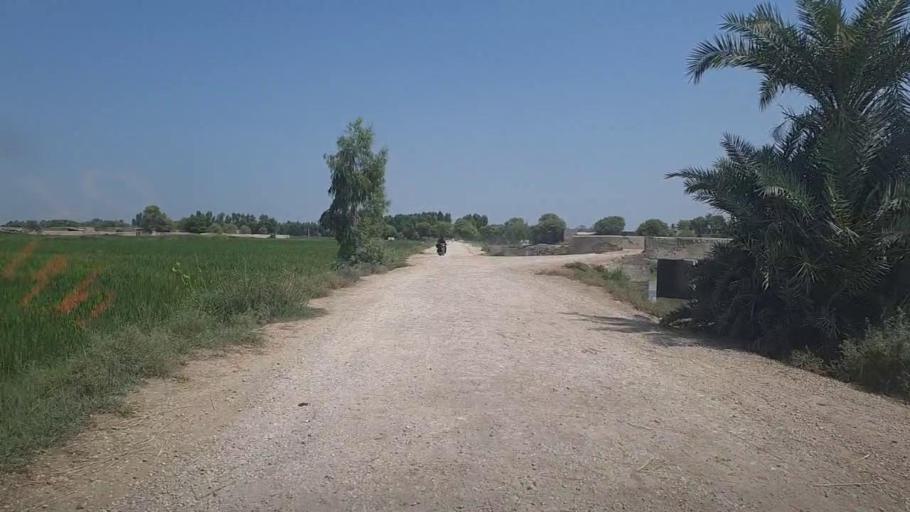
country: PK
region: Sindh
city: Kandhkot
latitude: 28.2708
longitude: 69.2248
